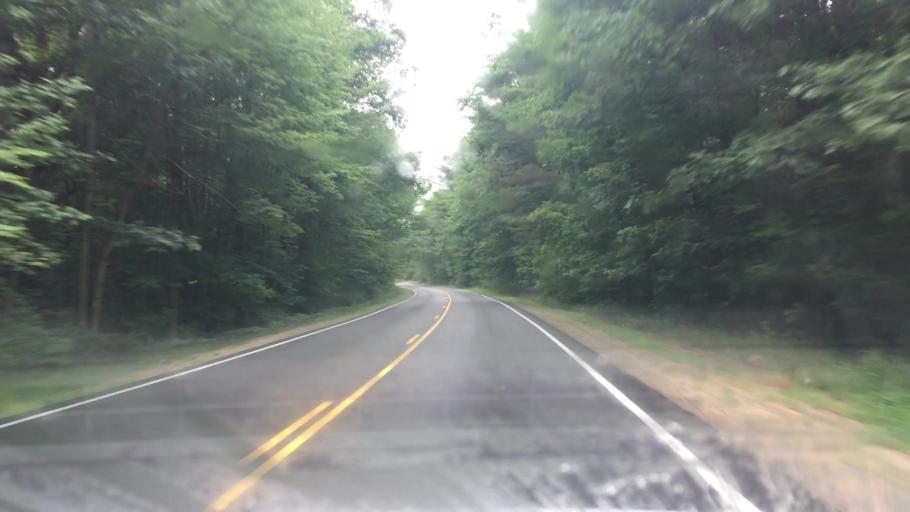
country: US
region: New York
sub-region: Clinton County
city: Morrisonville
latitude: 44.6243
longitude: -73.5975
